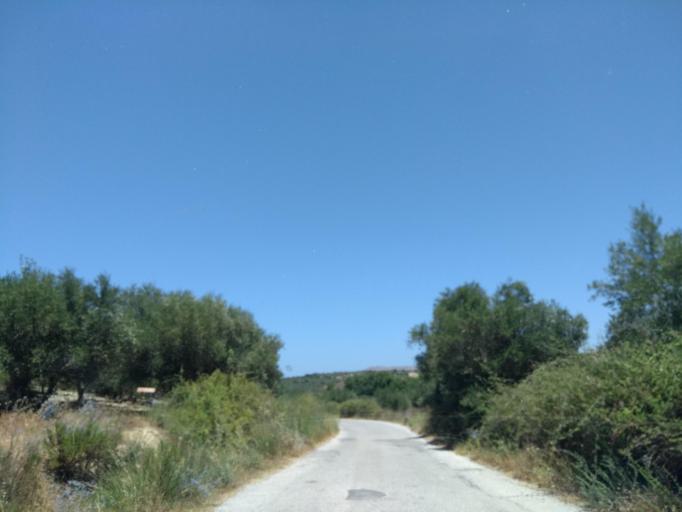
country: GR
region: Crete
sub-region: Nomos Chanias
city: Georgioupolis
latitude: 35.3263
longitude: 24.3169
